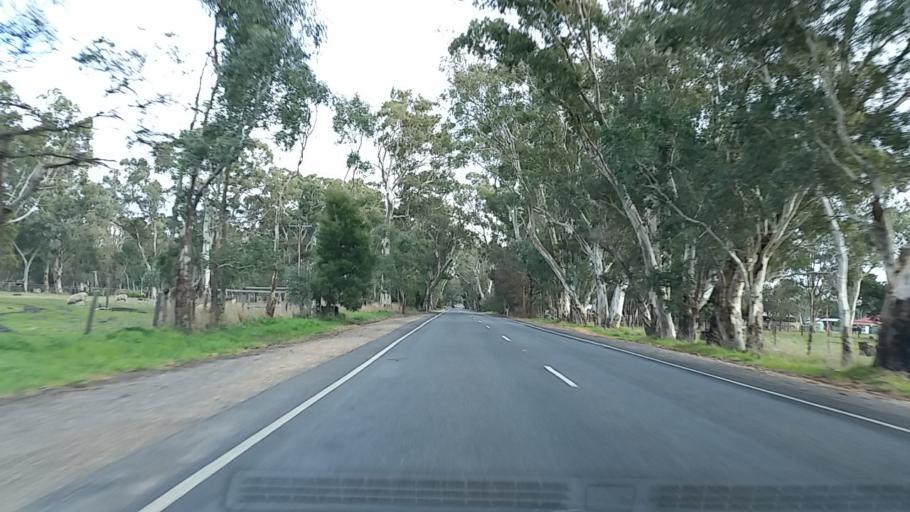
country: AU
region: South Australia
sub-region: Mount Barker
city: Meadows
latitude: -35.1973
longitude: 138.7230
